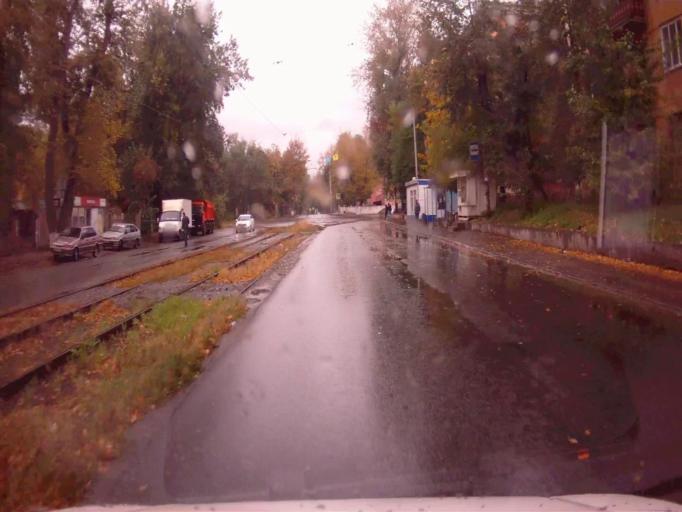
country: RU
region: Chelyabinsk
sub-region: Gorod Chelyabinsk
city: Chelyabinsk
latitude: 55.1904
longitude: 61.4126
